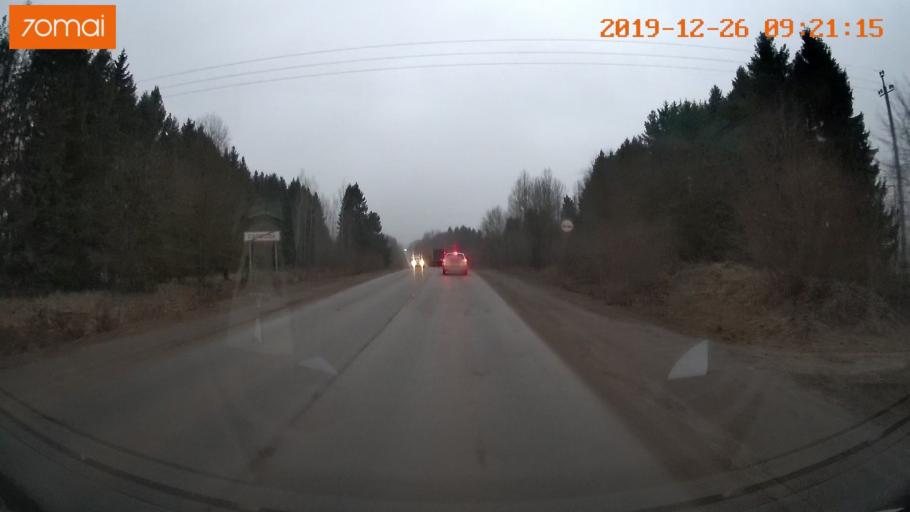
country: RU
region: Vologda
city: Gryazovets
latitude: 58.9689
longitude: 40.2254
